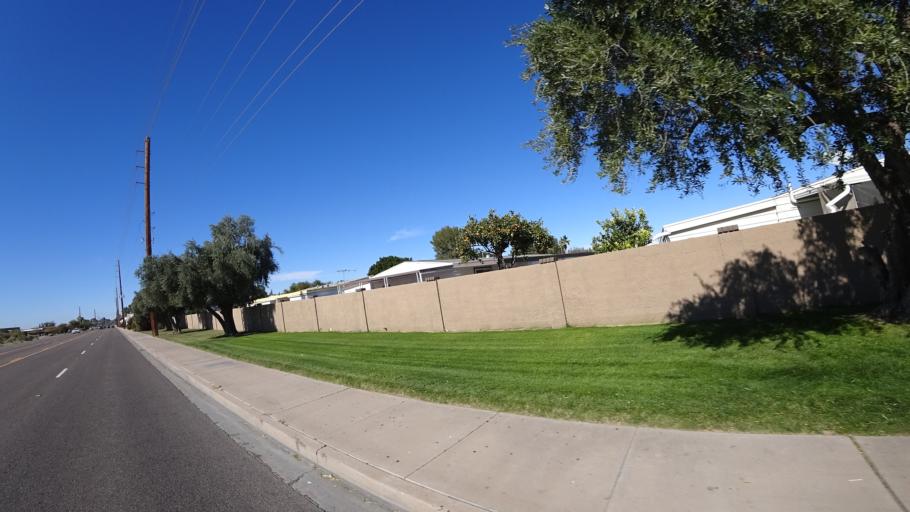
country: US
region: Arizona
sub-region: Maricopa County
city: Tempe
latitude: 33.4514
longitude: -111.9041
